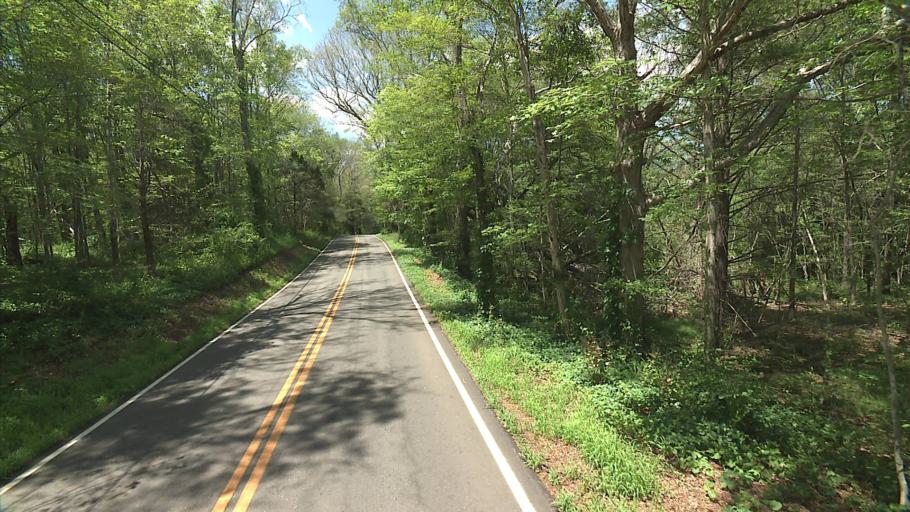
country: US
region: Connecticut
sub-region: Middlesex County
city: Essex Village
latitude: 41.4467
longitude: -72.3375
